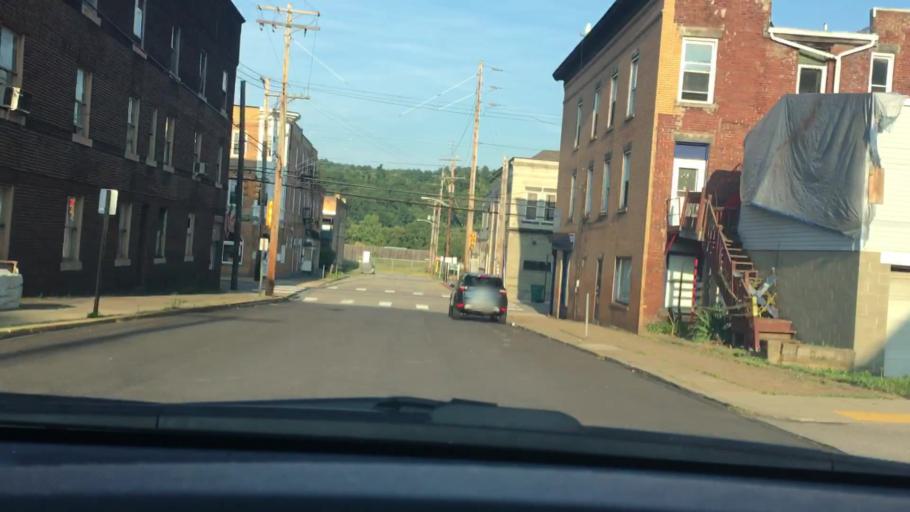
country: US
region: Pennsylvania
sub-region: Allegheny County
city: Glassport
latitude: 40.3277
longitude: -79.8919
